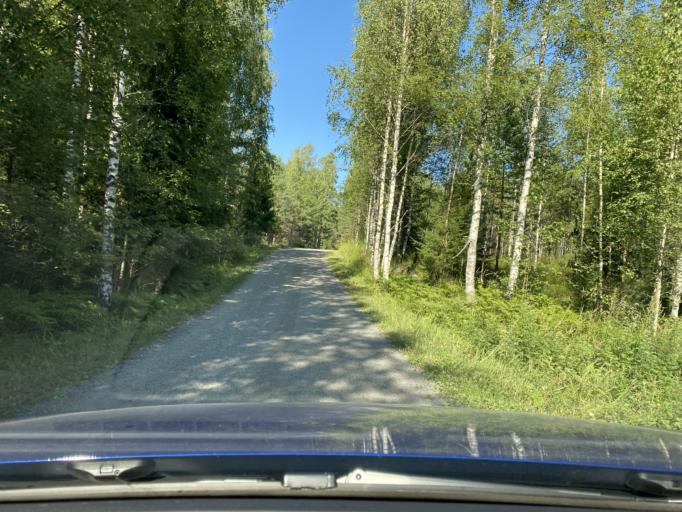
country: FI
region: Satakunta
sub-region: Rauma
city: Kiukainen
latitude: 61.1363
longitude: 22.0220
